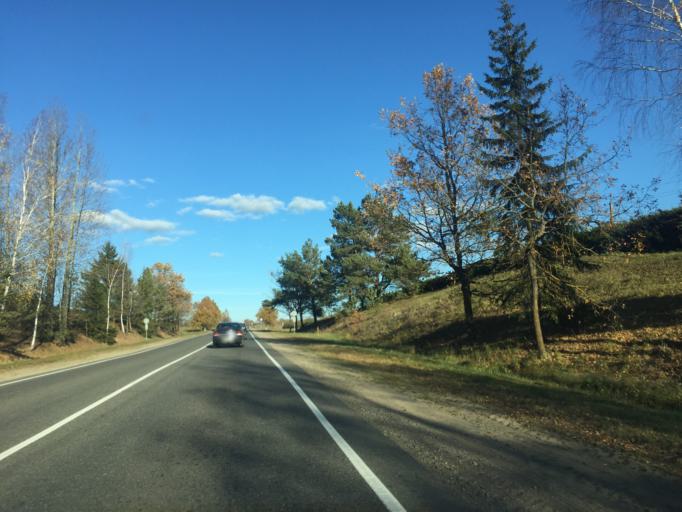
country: BY
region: Vitebsk
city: Dzisna
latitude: 55.2534
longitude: 28.1098
